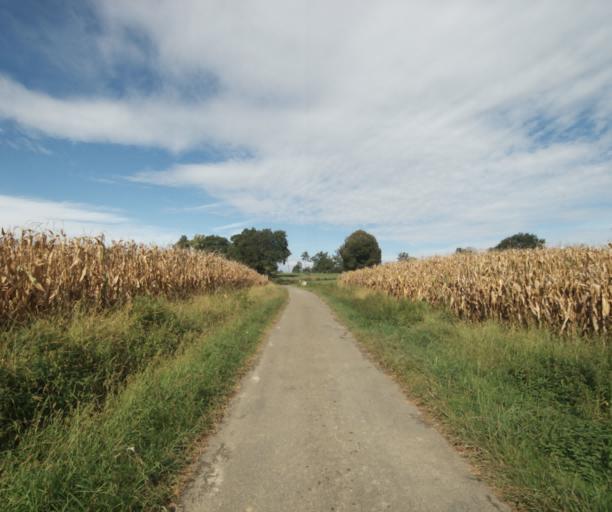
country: FR
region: Midi-Pyrenees
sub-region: Departement du Gers
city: Cazaubon
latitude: 43.9025
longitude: -0.1858
